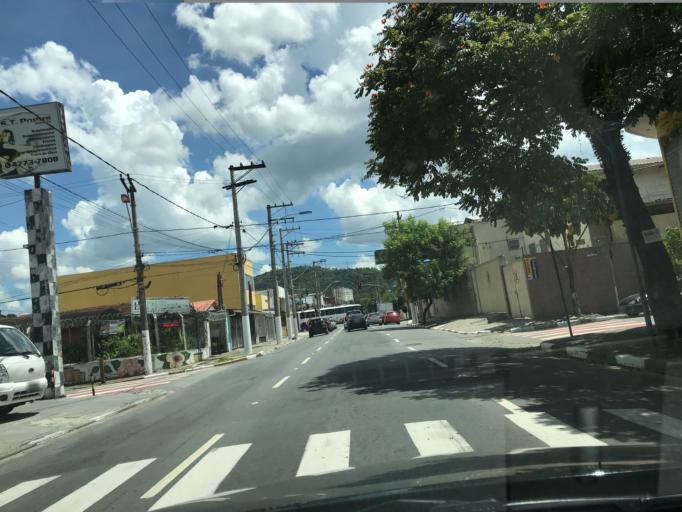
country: BR
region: Sao Paulo
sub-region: Itapevi
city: Itapevi
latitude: -23.5386
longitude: -46.9346
